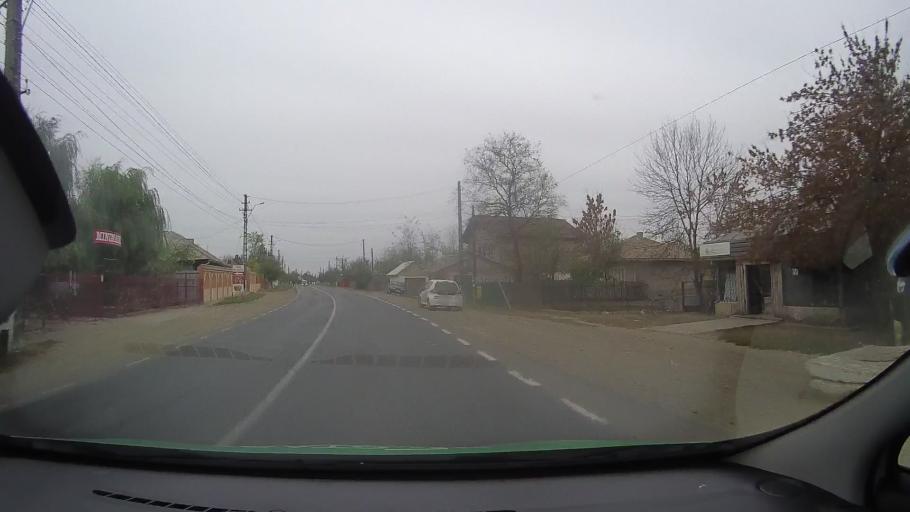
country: RO
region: Braila
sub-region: Comuna Baraganul
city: Baraganul
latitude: 44.8105
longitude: 27.5137
